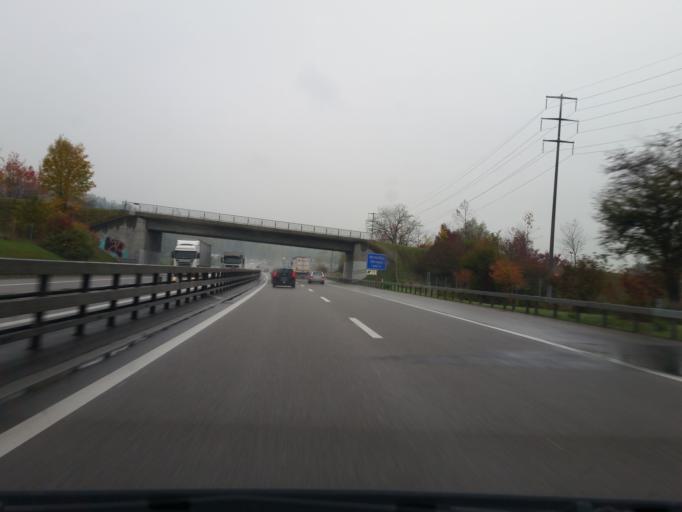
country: CH
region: Zurich
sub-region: Bezirk Winterthur
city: Seuzach / Seuzach (Dorf)
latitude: 47.5292
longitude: 8.7437
